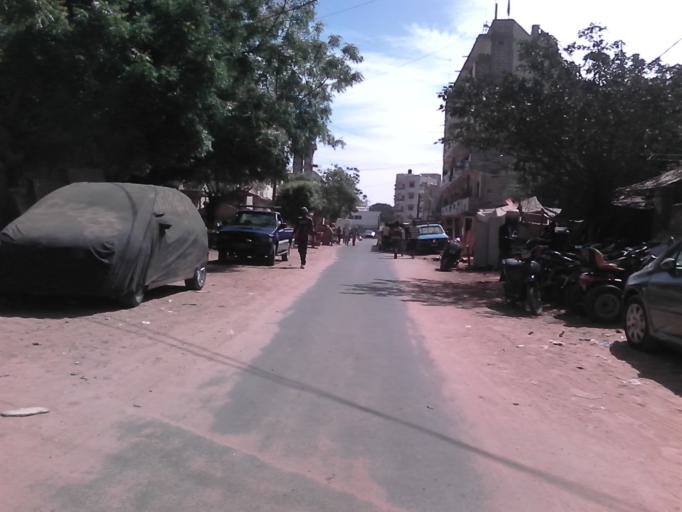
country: SN
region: Dakar
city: Grand Dakar
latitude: 14.7109
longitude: -17.4554
